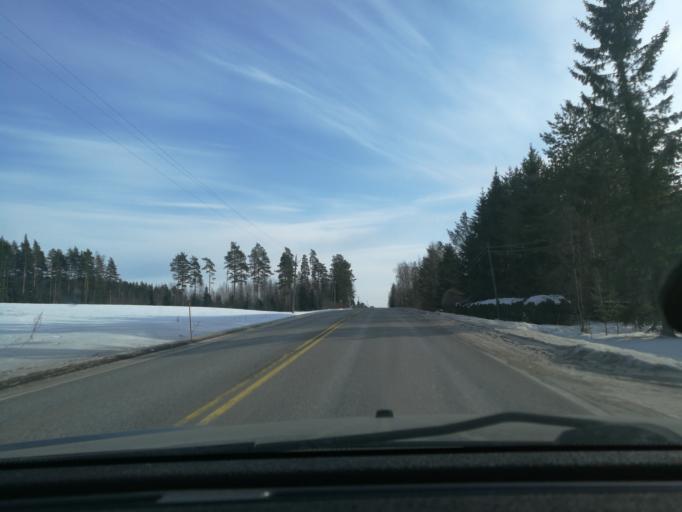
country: FI
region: Uusimaa
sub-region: Helsinki
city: Saukkola
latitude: 60.3995
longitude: 24.0668
